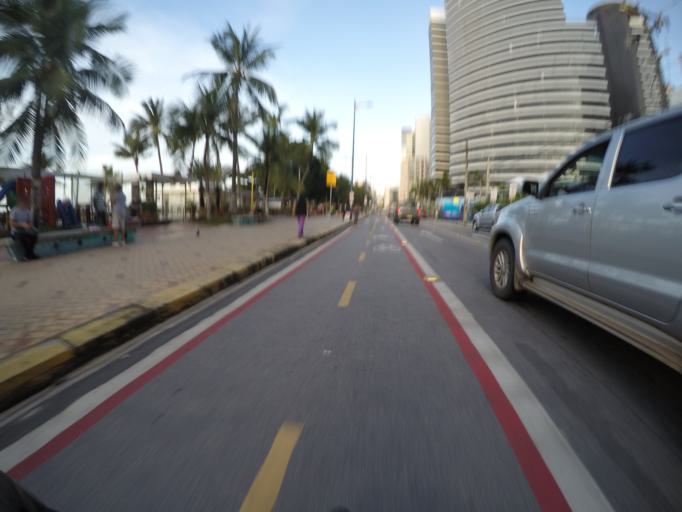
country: BR
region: Ceara
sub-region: Fortaleza
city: Fortaleza
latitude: -3.7252
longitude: -38.4996
